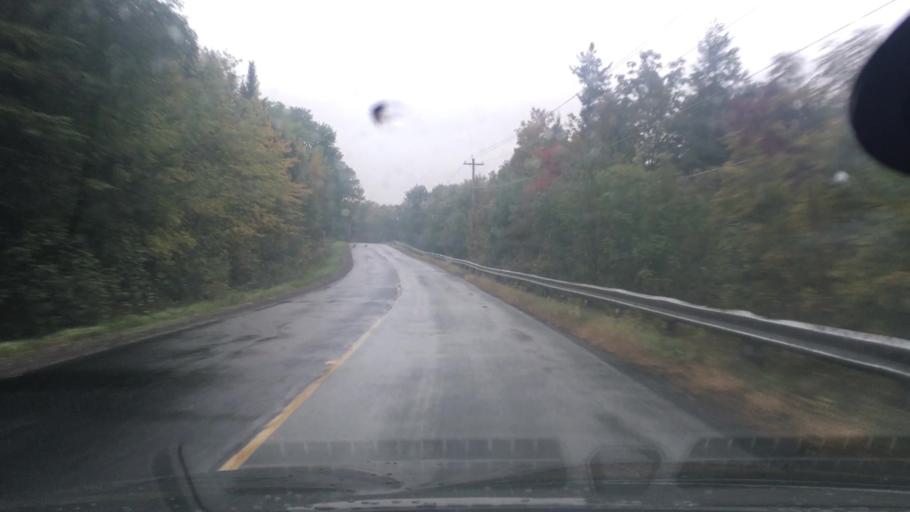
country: CA
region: Nova Scotia
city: Windsor
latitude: 44.8336
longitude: -64.2579
